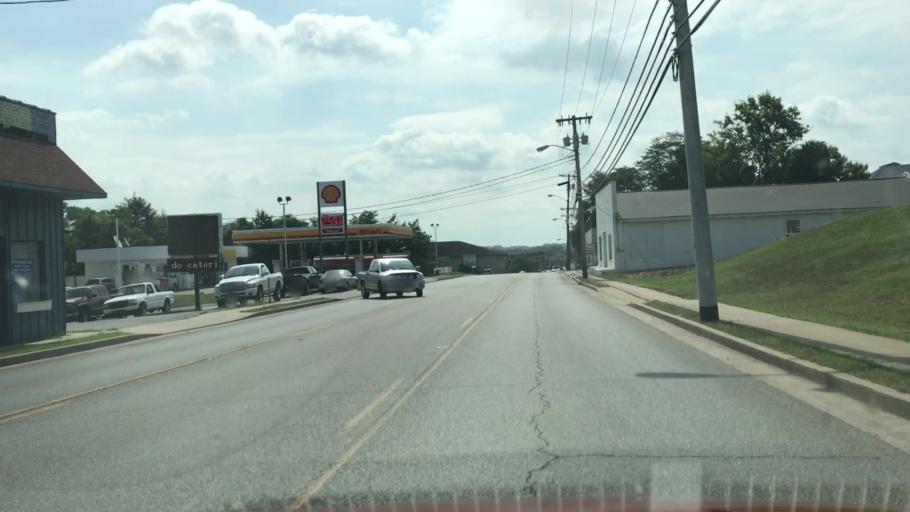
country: US
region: Kentucky
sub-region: Barren County
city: Glasgow
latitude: 36.9985
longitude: -85.9189
